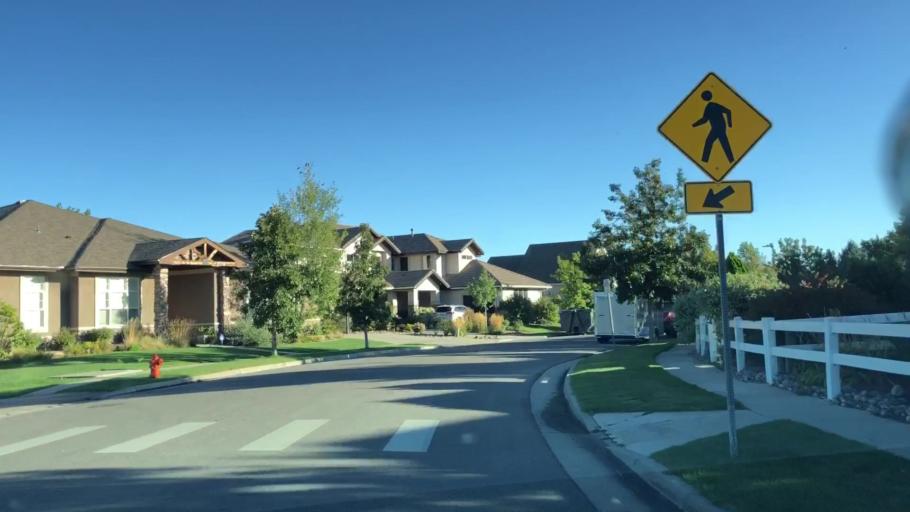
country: US
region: Colorado
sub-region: Larimer County
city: Loveland
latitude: 40.4399
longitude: -105.0281
